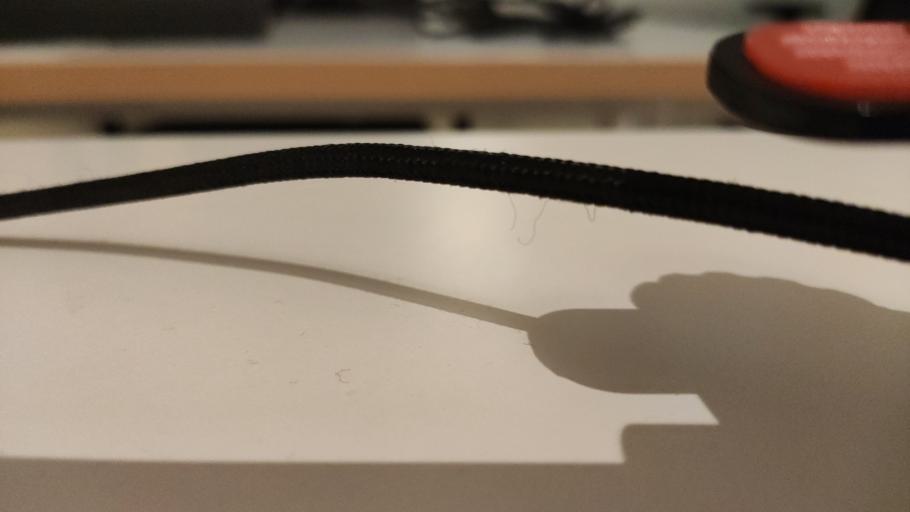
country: RU
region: Moskovskaya
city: Rybnoye
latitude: 56.4166
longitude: 37.6951
